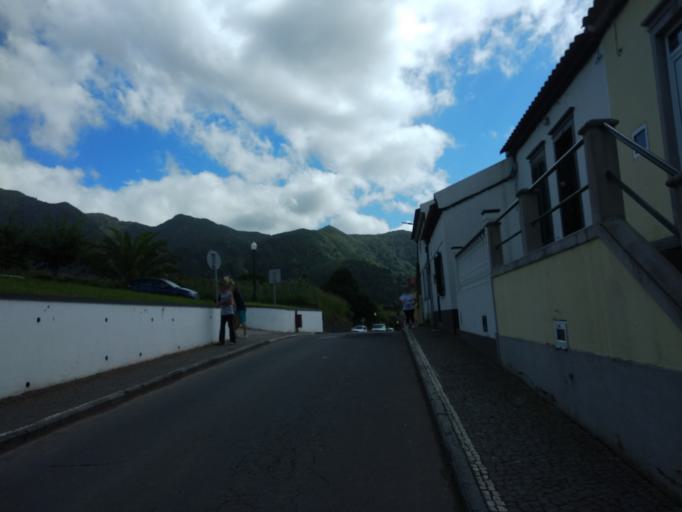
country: PT
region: Azores
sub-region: Povoacao
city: Furnas
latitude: 37.7731
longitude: -25.3066
